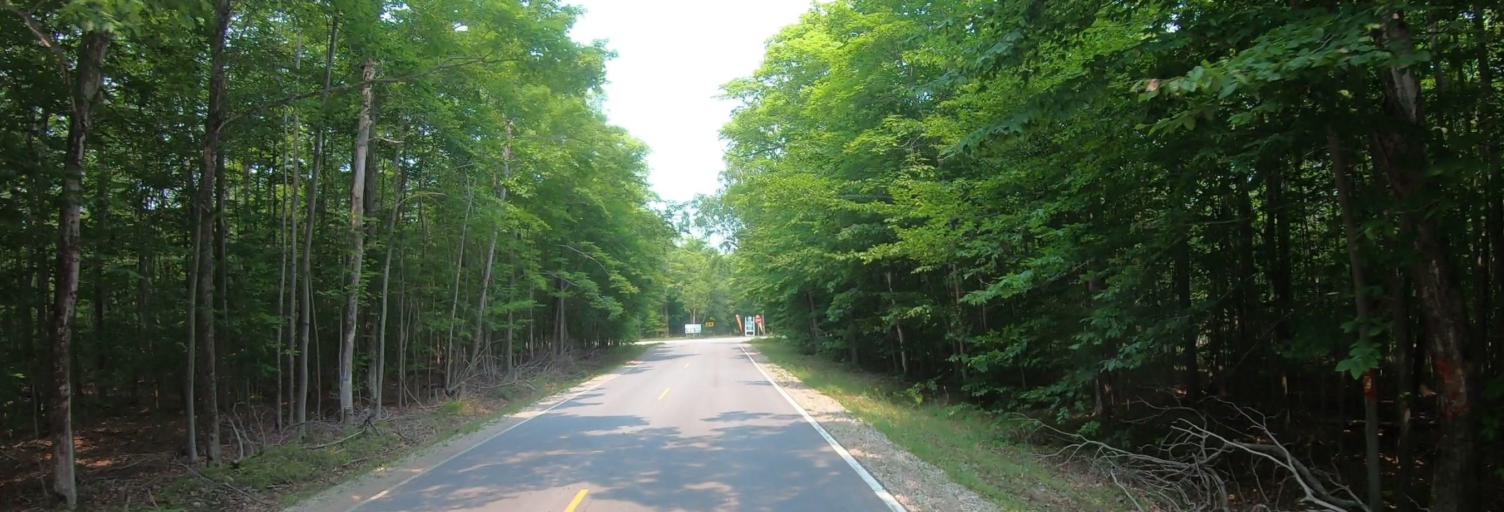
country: CA
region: Ontario
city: Thessalon
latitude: 46.0121
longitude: -83.6976
